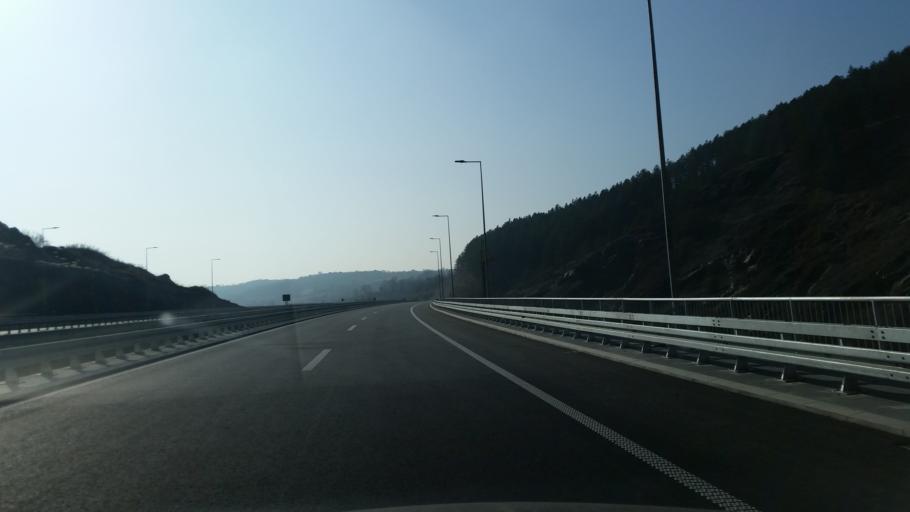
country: RS
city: Prislonica
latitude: 43.9768
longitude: 20.4006
